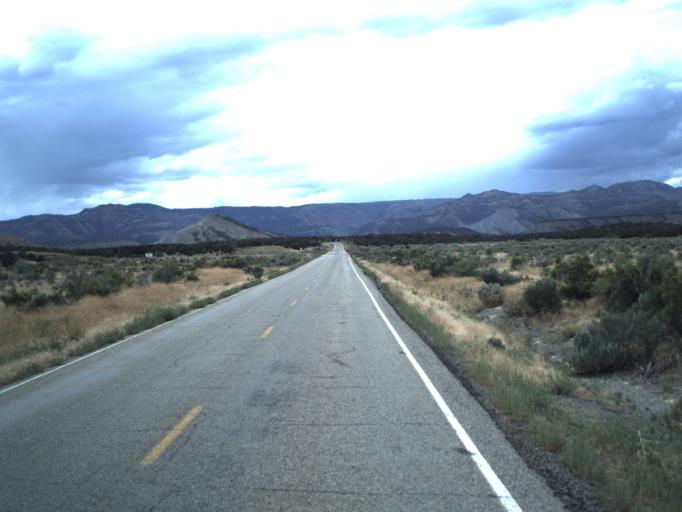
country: US
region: Utah
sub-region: Carbon County
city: Price
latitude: 39.4844
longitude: -110.8995
